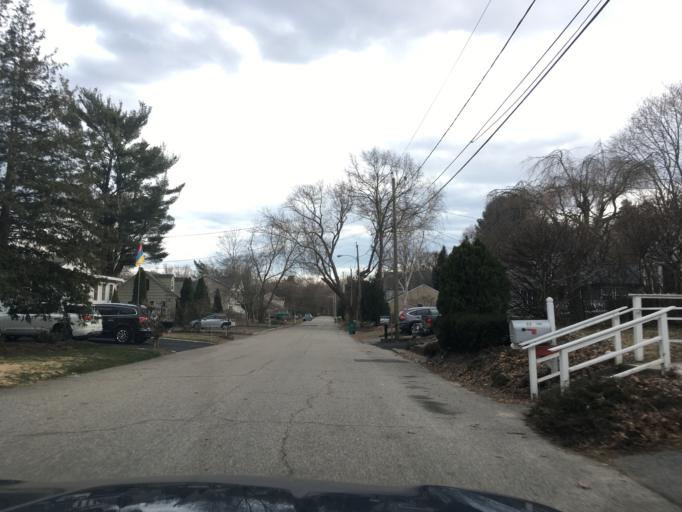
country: US
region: Rhode Island
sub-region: Kent County
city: Warwick
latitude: 41.6681
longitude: -71.4238
